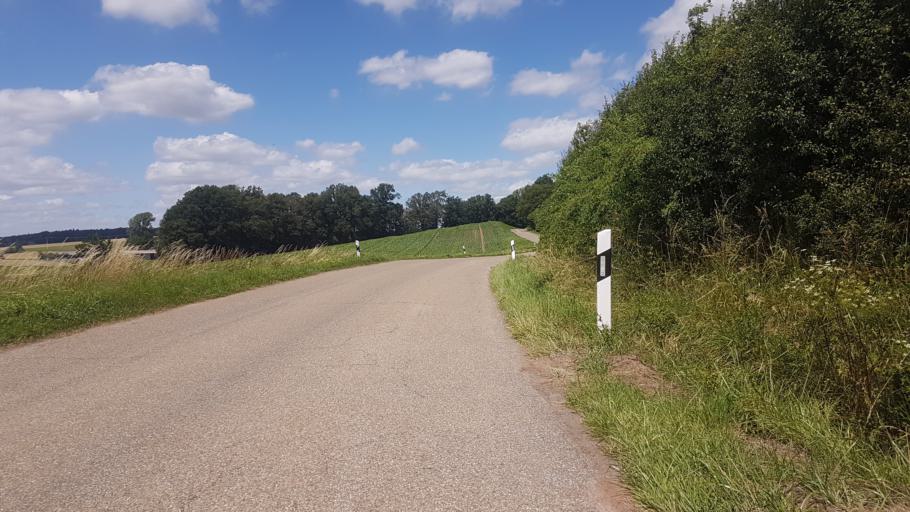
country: DE
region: Bavaria
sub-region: Regierungsbezirk Mittelfranken
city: Colmberg
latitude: 49.3318
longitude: 10.3755
